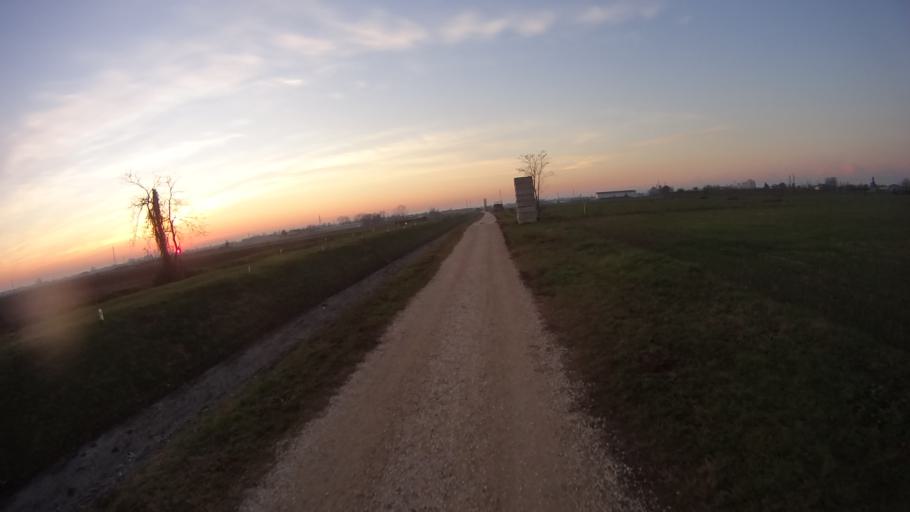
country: IT
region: Veneto
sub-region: Provincia di Verona
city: Povegliano Veronese
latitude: 45.3393
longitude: 10.8721
